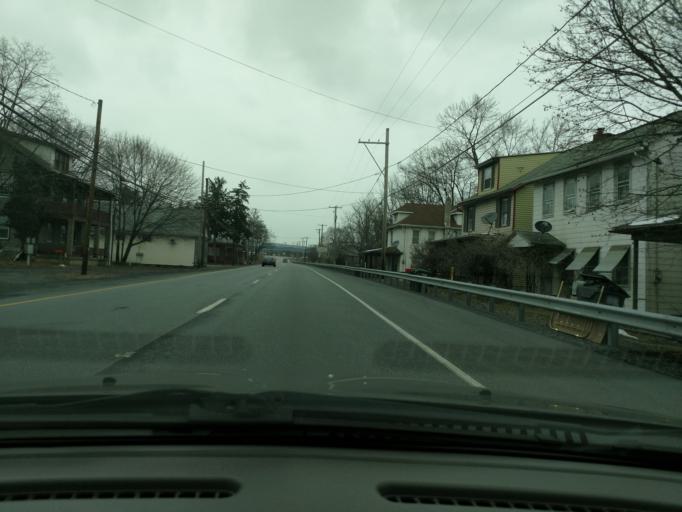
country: US
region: Pennsylvania
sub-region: Schuylkill County
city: Orwigsburg
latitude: 40.6256
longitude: -76.0610
